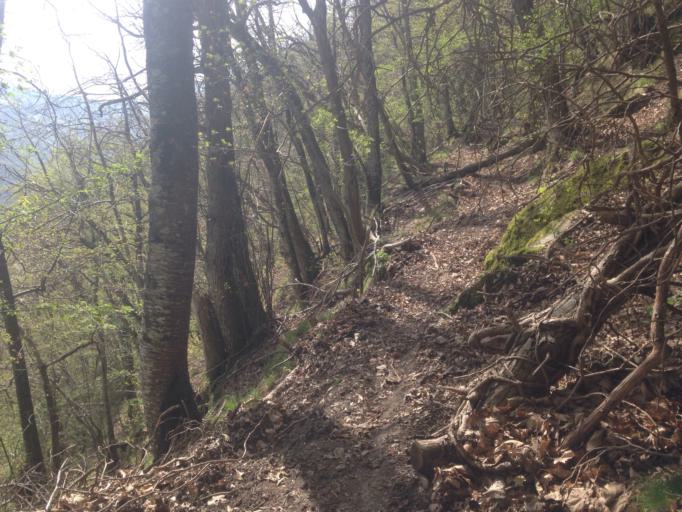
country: IT
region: Emilia-Romagna
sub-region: Provincia di Bologna
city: Lizzano in Belvedere
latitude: 44.1580
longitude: 10.8884
